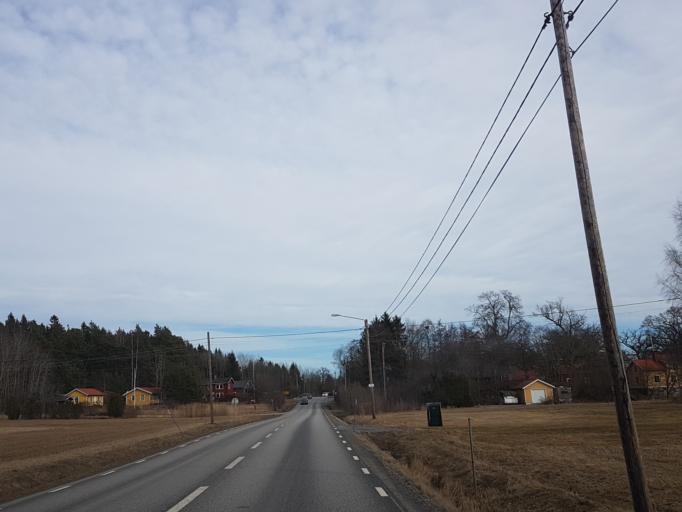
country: SE
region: Stockholm
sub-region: Norrtalje Kommun
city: Norrtalje
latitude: 59.6792
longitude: 18.7376
